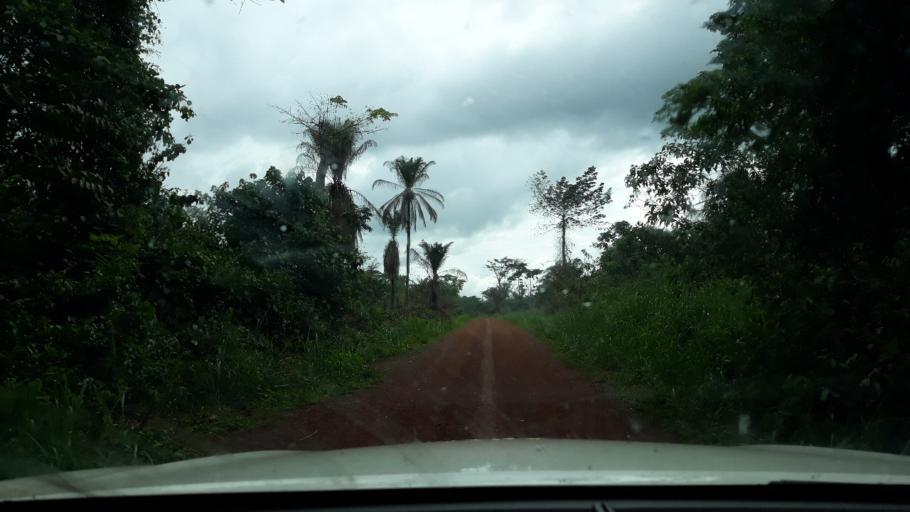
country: CD
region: Equateur
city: Libenge
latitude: 3.6981
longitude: 18.7496
